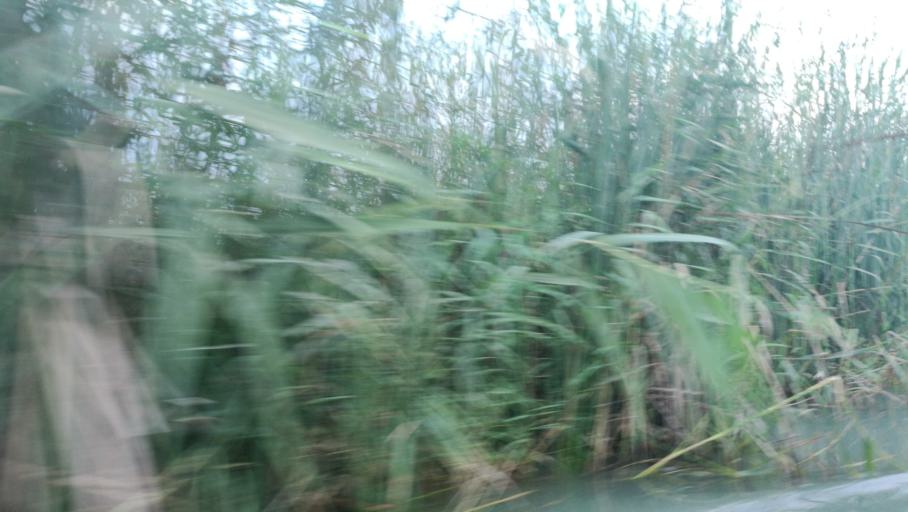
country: IQ
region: Dhi Qar
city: Al Jabayish
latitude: 30.9826
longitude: 47.0426
